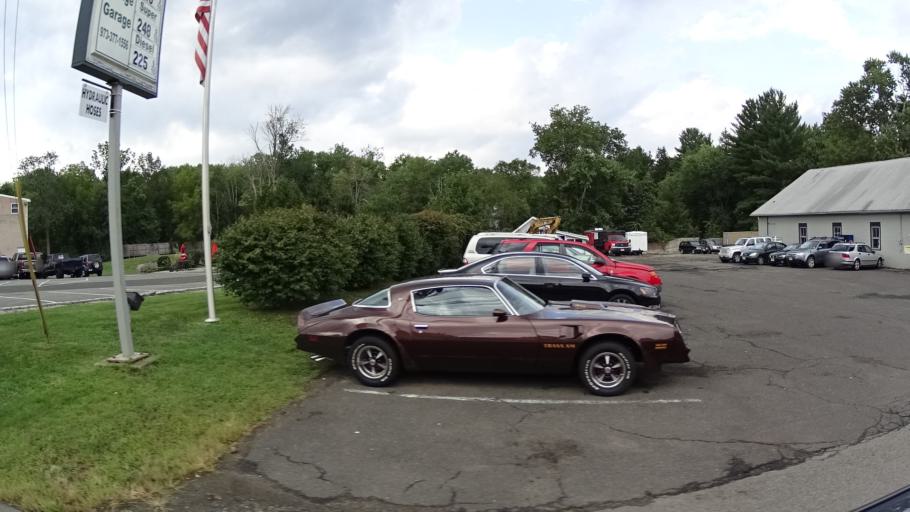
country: US
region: New Jersey
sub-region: Morris County
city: Madison
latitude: 40.7389
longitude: -74.4526
